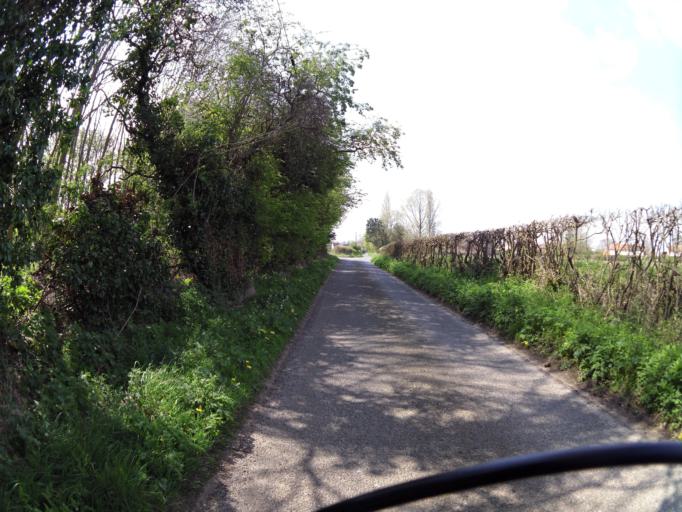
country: GB
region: England
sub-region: Suffolk
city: Hadleigh
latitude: 52.0818
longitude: 0.9603
